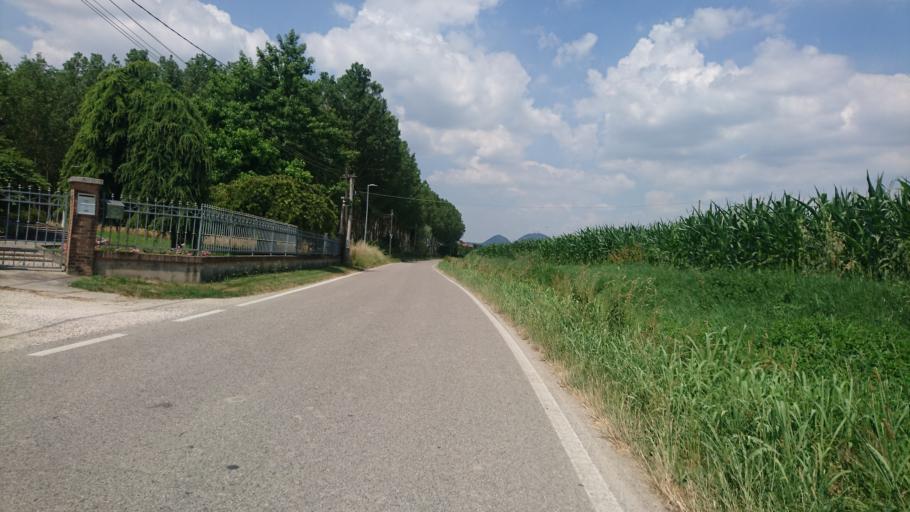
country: IT
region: Veneto
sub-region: Provincia di Padova
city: Sant'Elena
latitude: 45.1988
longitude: 11.7254
